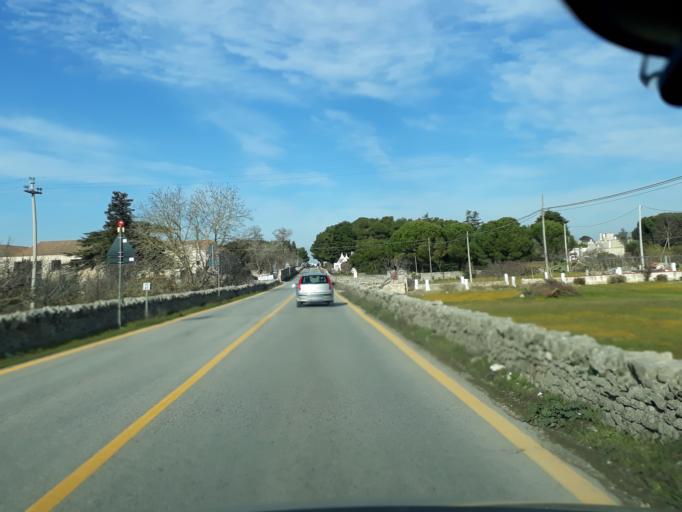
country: IT
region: Apulia
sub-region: Provincia di Taranto
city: Martina Franca
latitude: 40.7191
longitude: 17.3327
